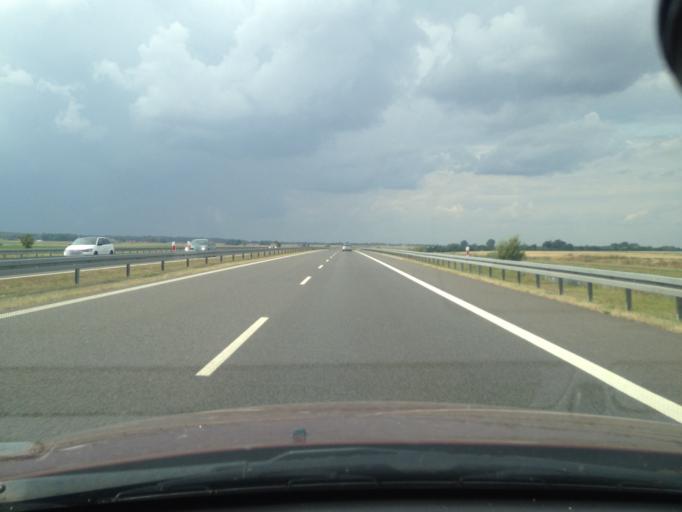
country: PL
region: West Pomeranian Voivodeship
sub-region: Powiat pyrzycki
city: Kozielice
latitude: 53.0992
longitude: 14.8006
